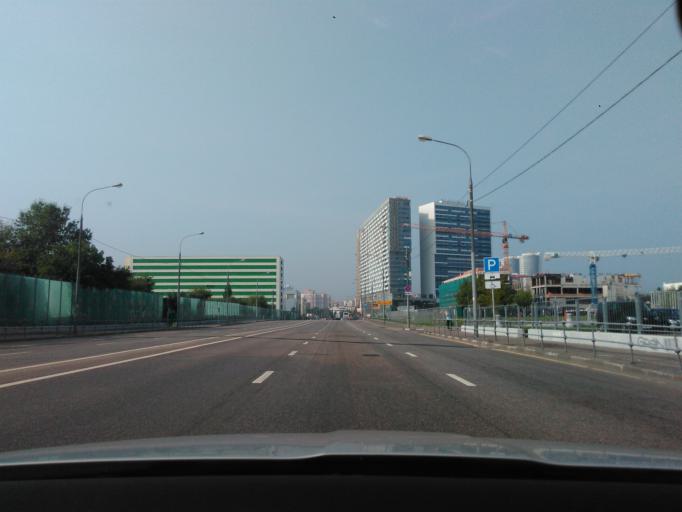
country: RU
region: Moscow
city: Sokol
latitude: 55.7898
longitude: 37.5479
